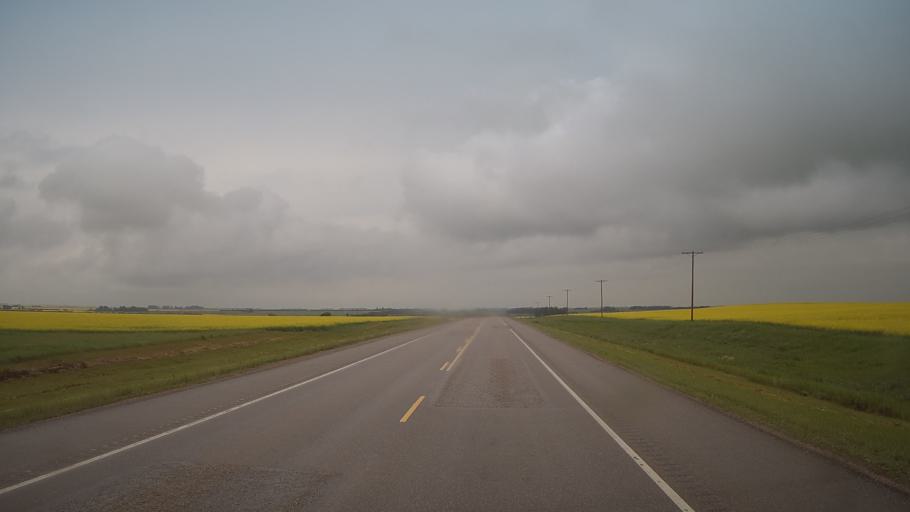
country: CA
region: Saskatchewan
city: Wilkie
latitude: 52.4291
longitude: -108.9163
